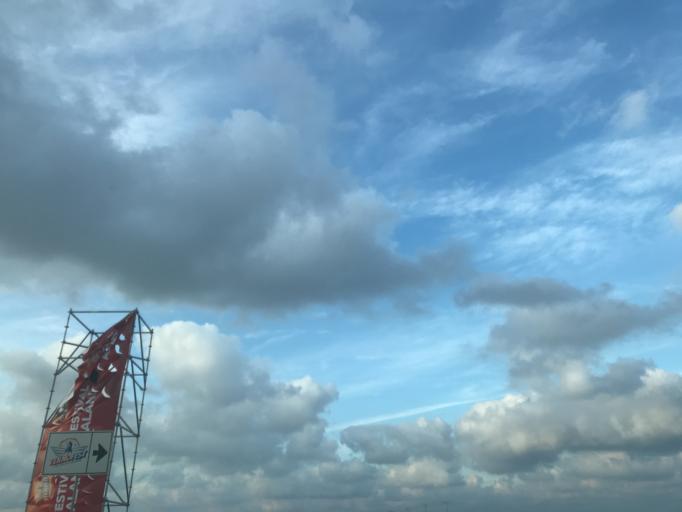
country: TR
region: Istanbul
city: Durusu
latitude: 41.2537
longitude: 28.7082
